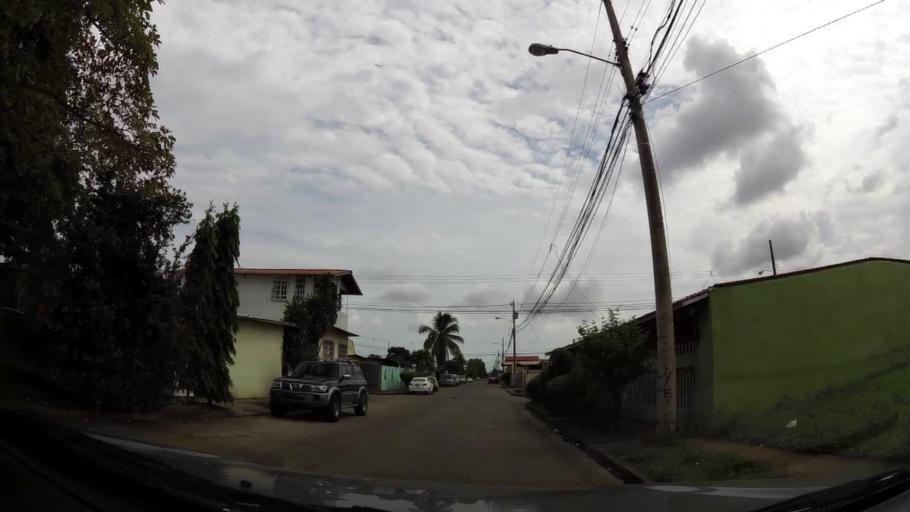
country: PA
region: Panama
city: Tocumen
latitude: 9.0497
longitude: -79.4161
